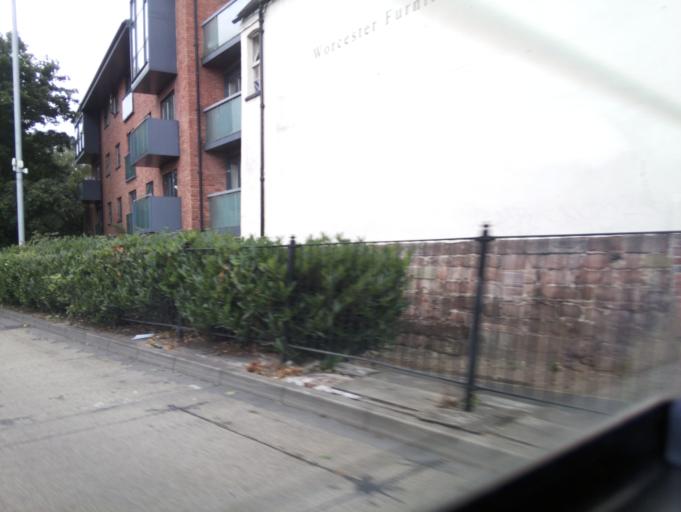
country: GB
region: England
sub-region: Worcestershire
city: Worcester
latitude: 52.1927
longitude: -2.2178
